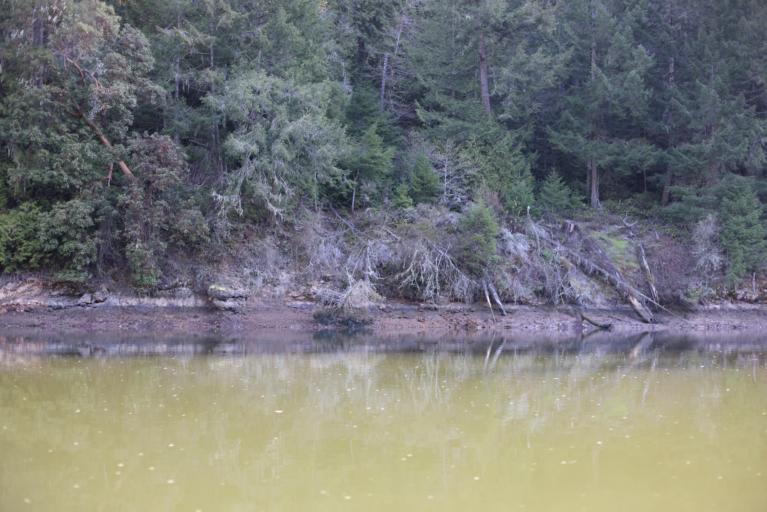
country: CA
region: British Columbia
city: Langford
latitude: 48.5619
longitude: -123.4741
